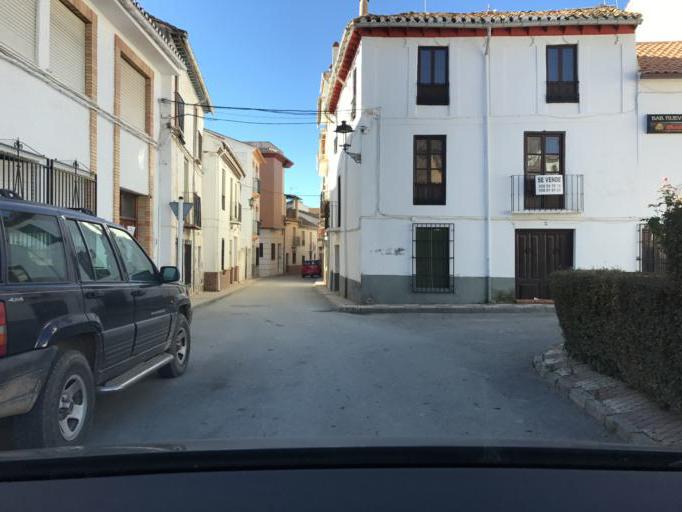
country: ES
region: Andalusia
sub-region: Provincia de Granada
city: Alfacar
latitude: 37.2365
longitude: -3.5708
